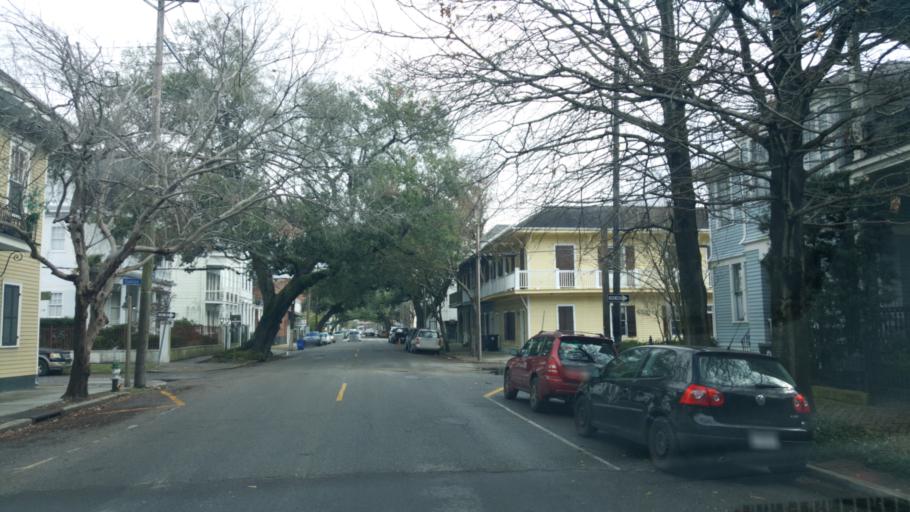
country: US
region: Louisiana
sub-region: Orleans Parish
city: New Orleans
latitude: 29.9365
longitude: -90.0755
